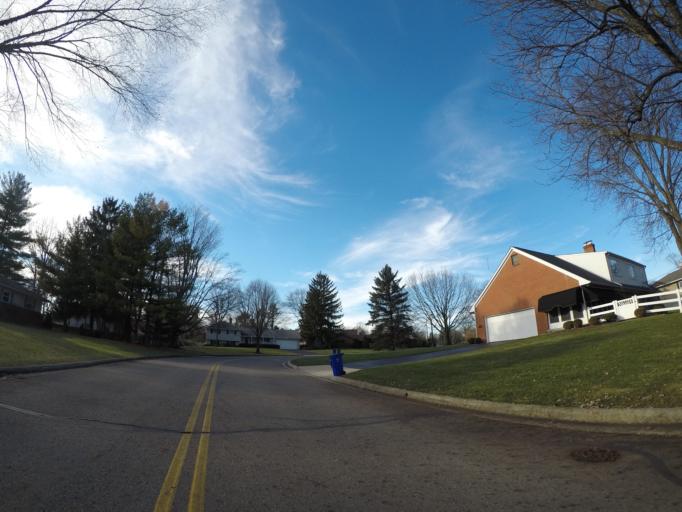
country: US
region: Ohio
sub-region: Franklin County
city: Upper Arlington
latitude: 40.0270
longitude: -83.0534
